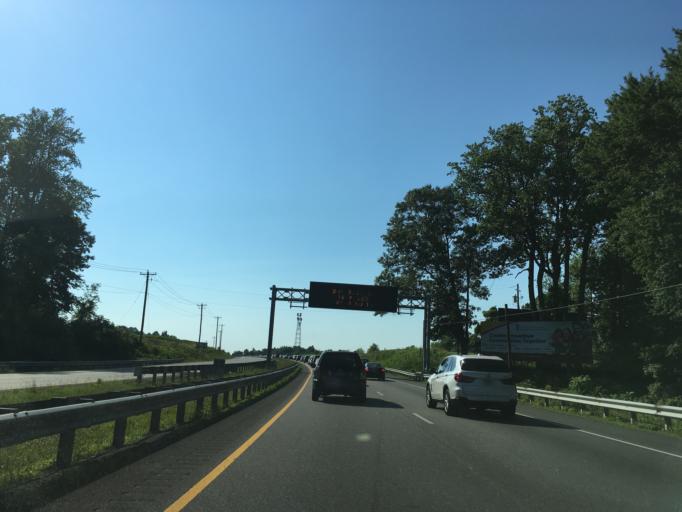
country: US
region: Maryland
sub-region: Queen Anne's County
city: Centreville
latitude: 38.9504
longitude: -76.0675
